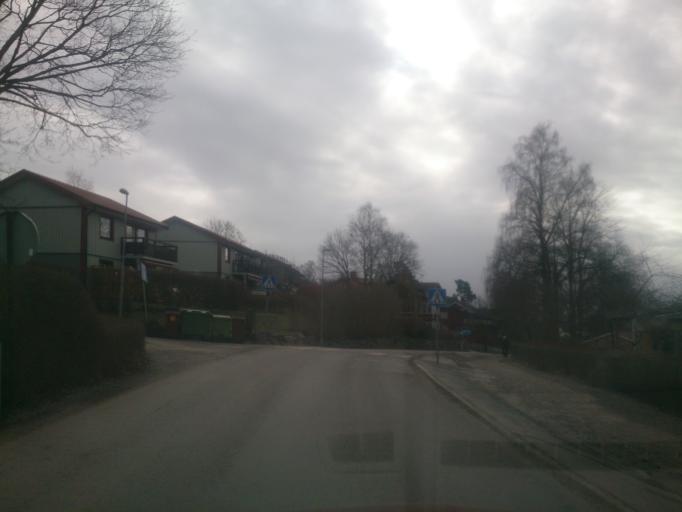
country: SE
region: OEstergoetland
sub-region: Norrkopings Kommun
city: Jursla
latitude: 58.6713
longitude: 16.1839
